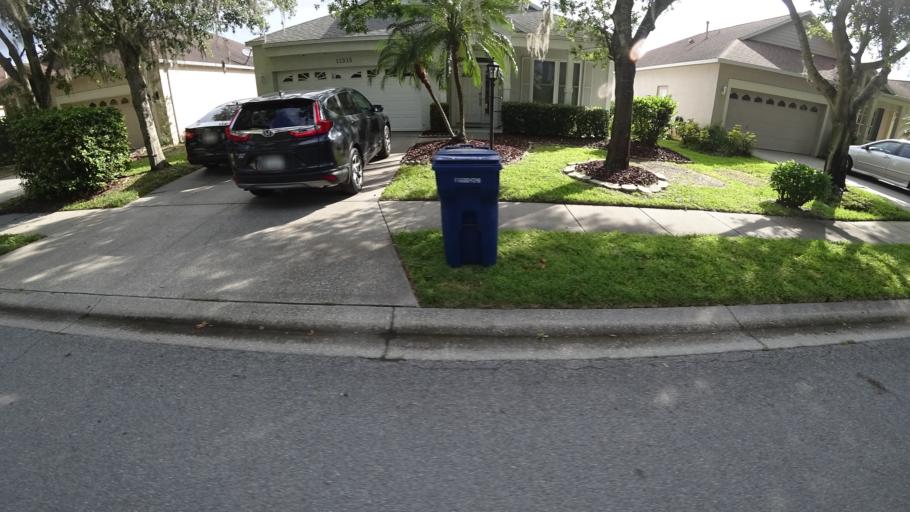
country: US
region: Florida
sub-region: Sarasota County
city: The Meadows
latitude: 27.4255
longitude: -82.4295
